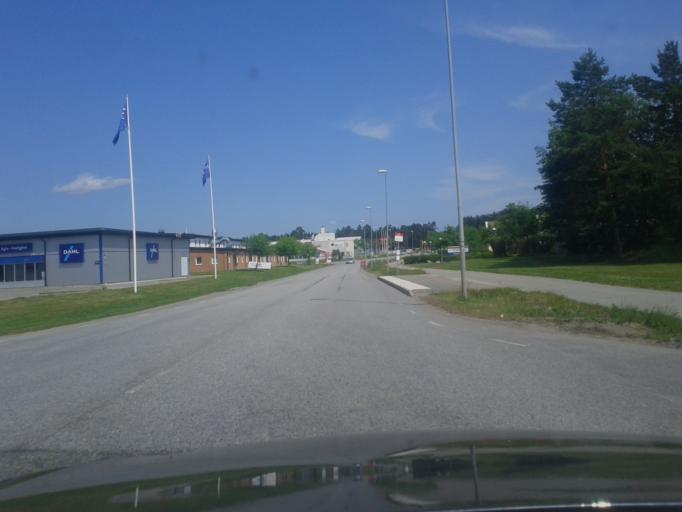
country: SE
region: Stockholm
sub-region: Taby Kommun
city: Taby
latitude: 59.4668
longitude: 18.1272
